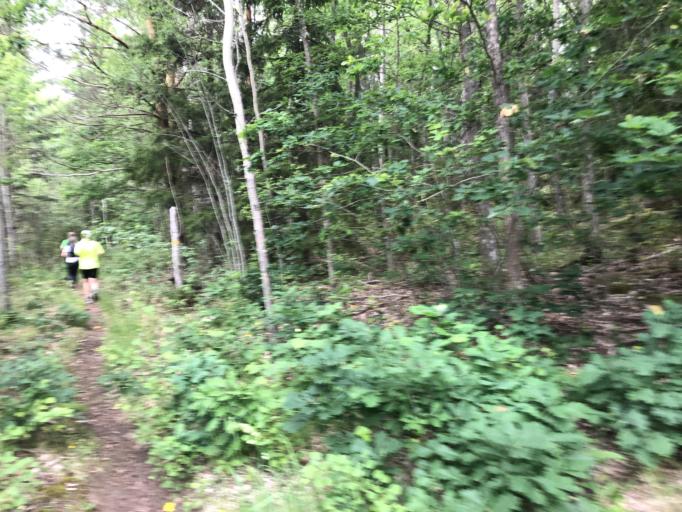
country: SE
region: Kalmar
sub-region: Vasterviks Kommun
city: Ankarsrum
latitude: 57.5157
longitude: 16.4650
